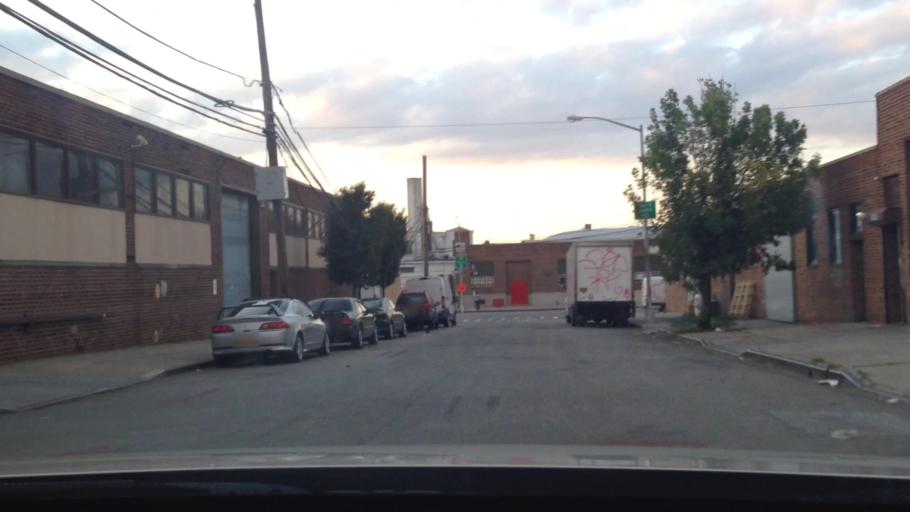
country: US
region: New York
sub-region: Queens County
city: Long Island City
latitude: 40.7179
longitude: -73.9148
